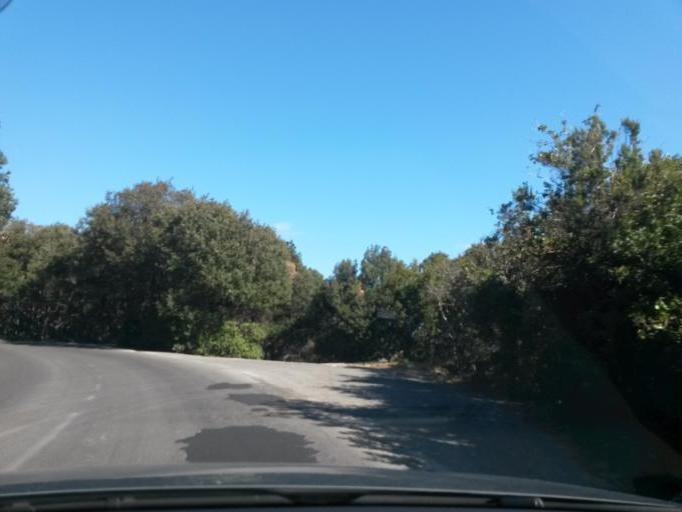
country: IT
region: Tuscany
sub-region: Provincia di Livorno
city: Marciana Marina
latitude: 42.7883
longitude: 10.2310
